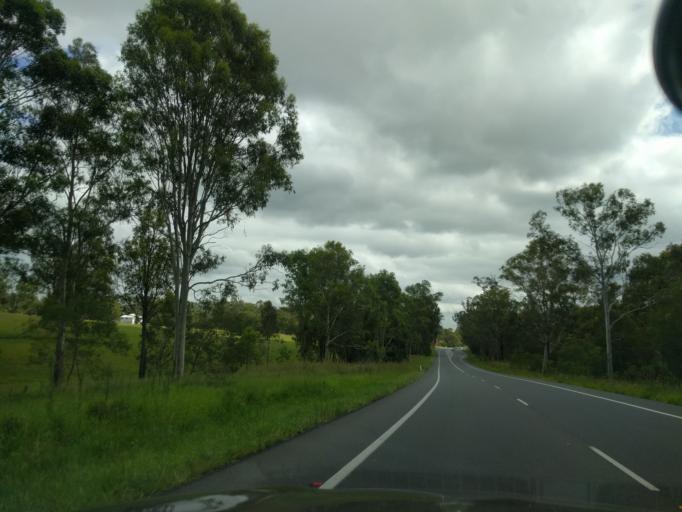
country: AU
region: Queensland
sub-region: Logan
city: Cedar Vale
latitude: -27.8684
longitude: 152.9990
